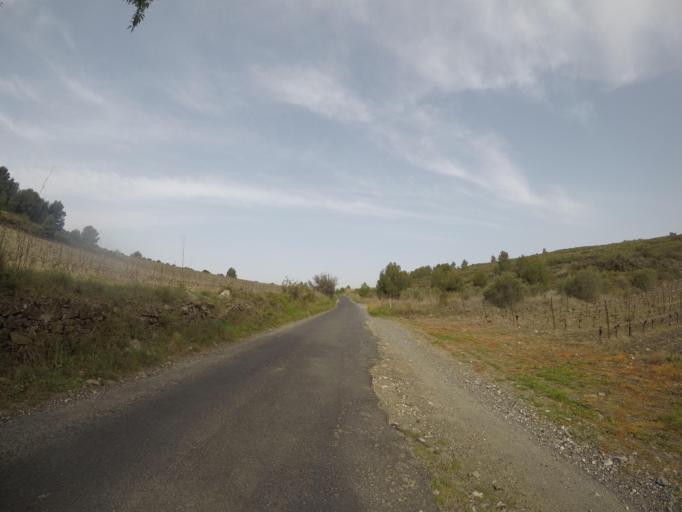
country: FR
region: Languedoc-Roussillon
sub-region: Departement des Pyrenees-Orientales
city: Baixas
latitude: 42.7701
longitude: 2.8058
